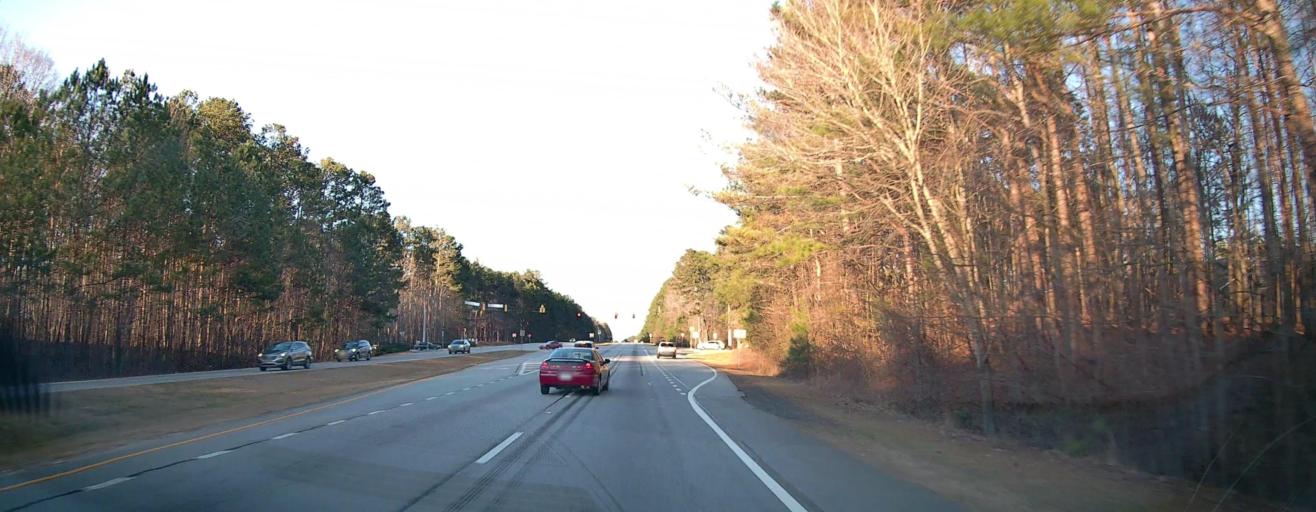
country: US
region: Georgia
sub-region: Fayette County
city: Tyrone
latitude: 33.4351
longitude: -84.5964
